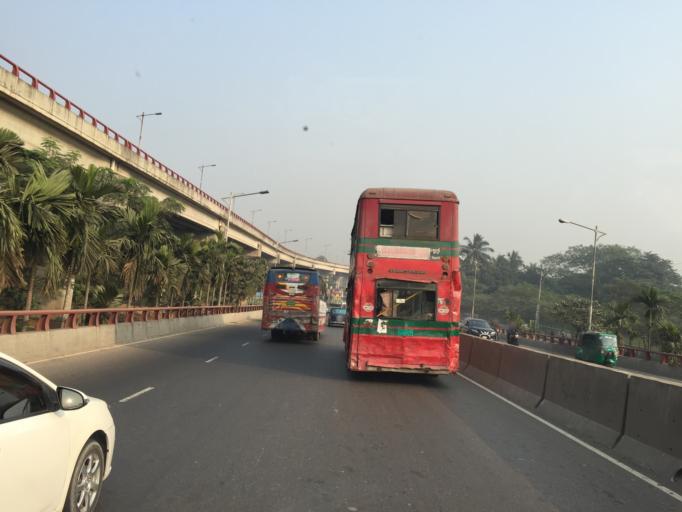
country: BD
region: Dhaka
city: Paltan
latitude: 23.8135
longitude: 90.4041
